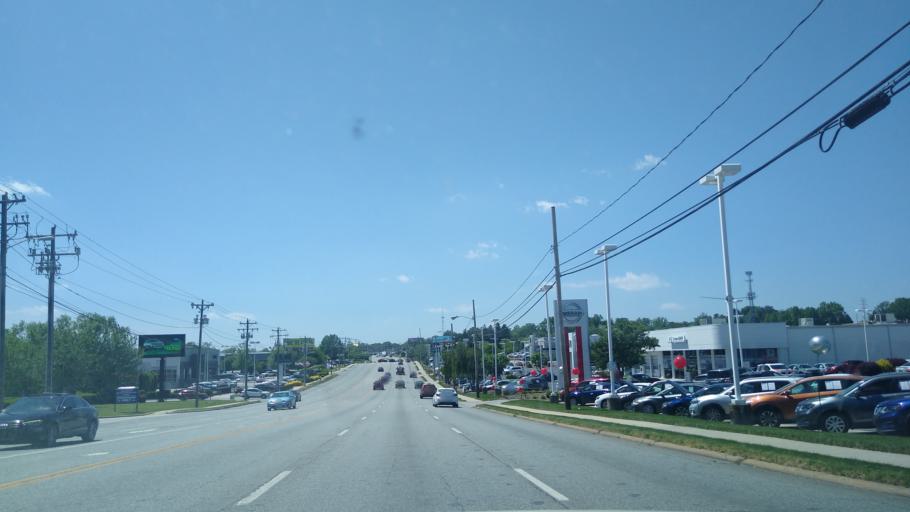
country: US
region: North Carolina
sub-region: Guilford County
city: Greensboro
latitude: 36.0600
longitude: -79.8762
